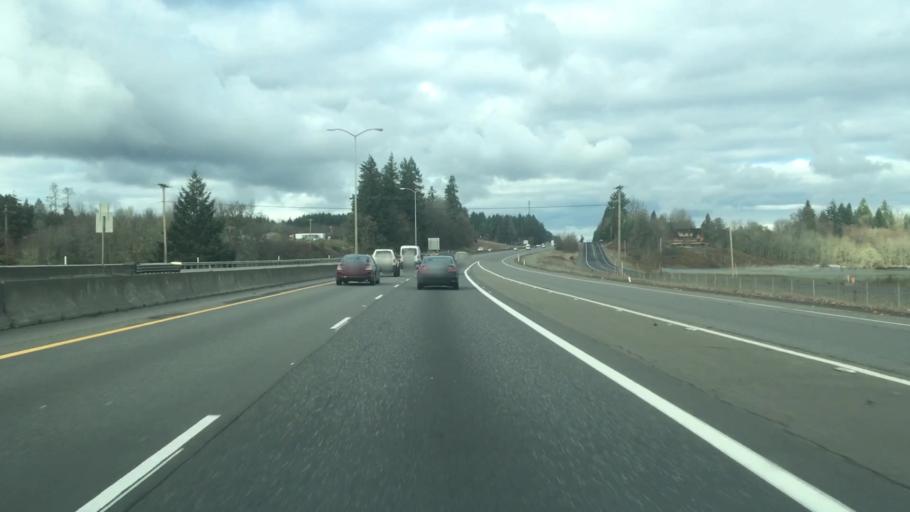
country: US
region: Washington
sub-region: Lewis County
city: Winlock
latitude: 46.4193
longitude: -122.8910
